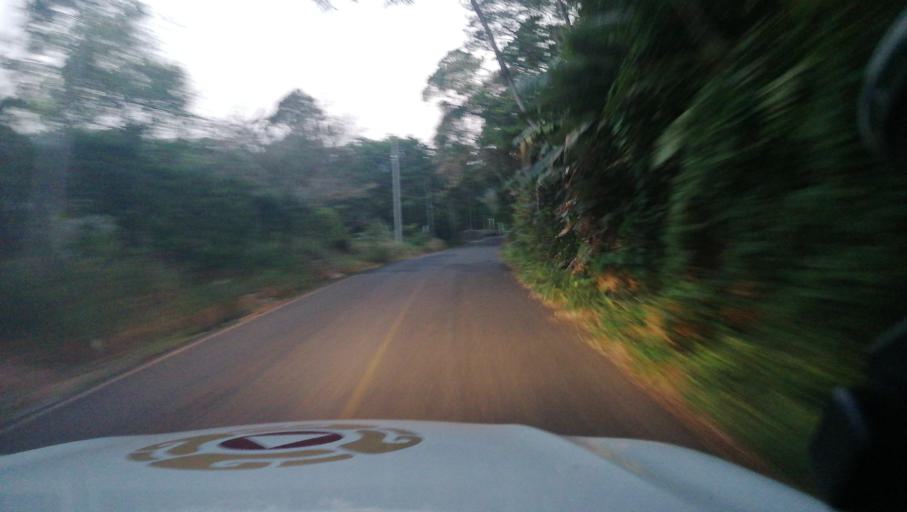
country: MX
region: Chiapas
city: Veinte de Noviembre
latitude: 14.9983
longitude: -92.2433
